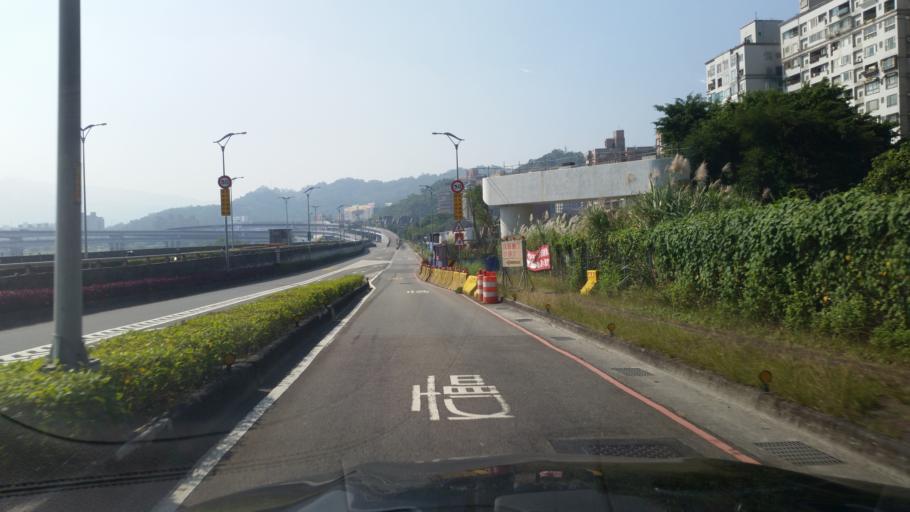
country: TW
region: Taipei
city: Taipei
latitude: 24.9860
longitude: 121.5230
